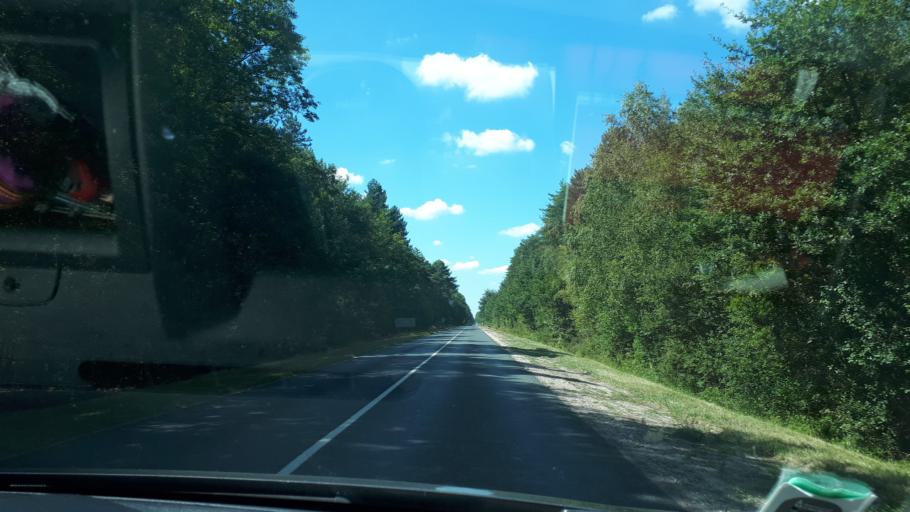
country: FR
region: Centre
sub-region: Departement du Loir-et-Cher
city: Neung-sur-Beuvron
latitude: 47.5389
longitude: 1.8434
